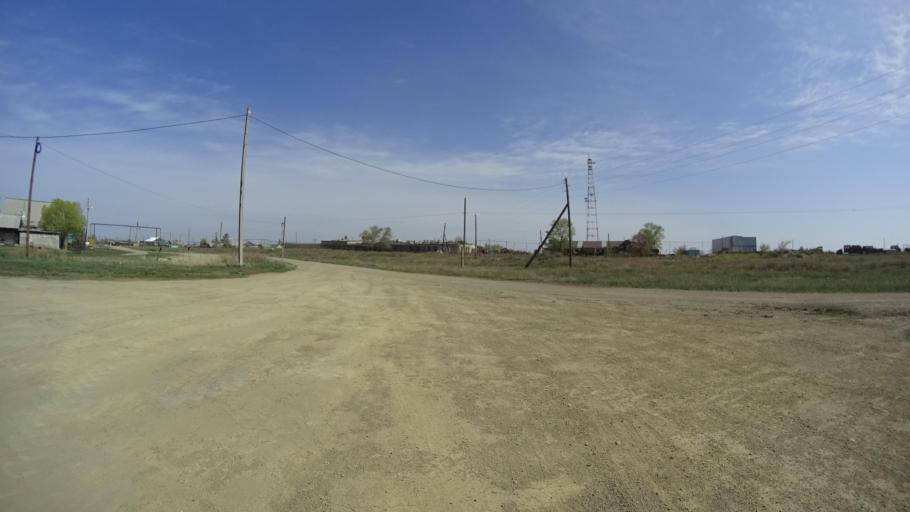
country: RU
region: Chelyabinsk
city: Chesma
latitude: 53.7872
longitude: 61.0396
